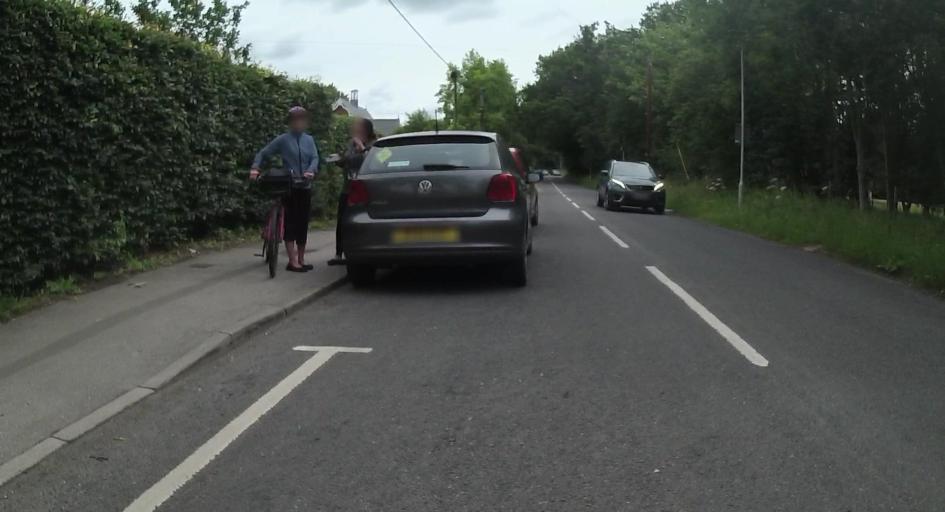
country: GB
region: England
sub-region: Wokingham
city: Winnersh
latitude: 51.4217
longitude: -0.8839
